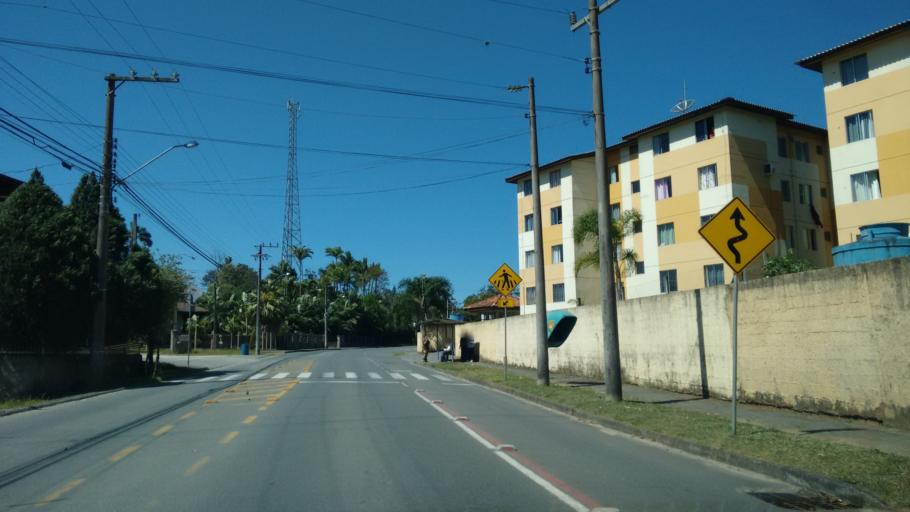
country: BR
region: Santa Catarina
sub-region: Blumenau
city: Blumenau
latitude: -26.8883
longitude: -49.1283
